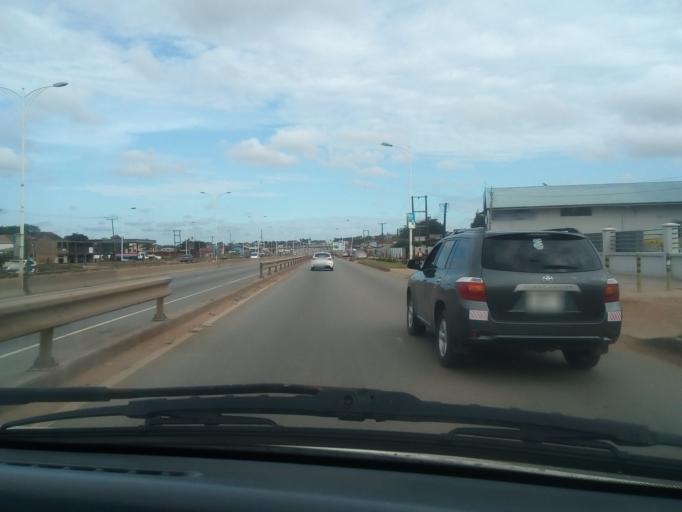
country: GH
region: Greater Accra
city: Dome
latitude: 5.6522
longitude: -0.2574
